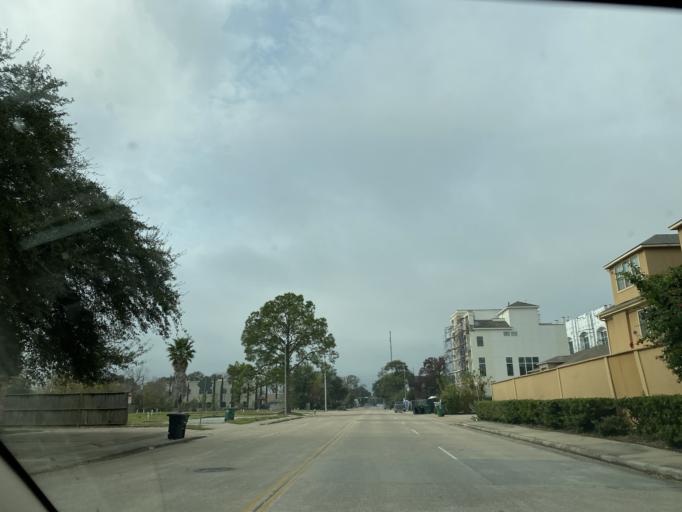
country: US
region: Texas
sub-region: Harris County
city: Bellaire
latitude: 29.7355
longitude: -95.4807
